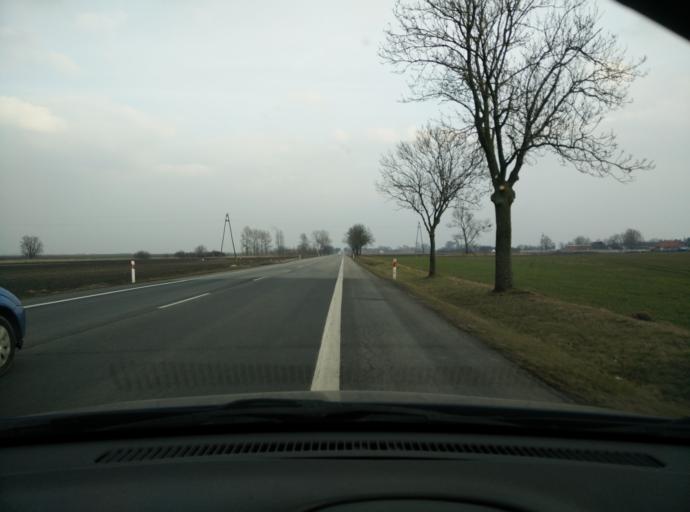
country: PL
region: Greater Poland Voivodeship
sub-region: Powiat poznanski
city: Kornik
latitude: 52.2404
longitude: 17.1479
